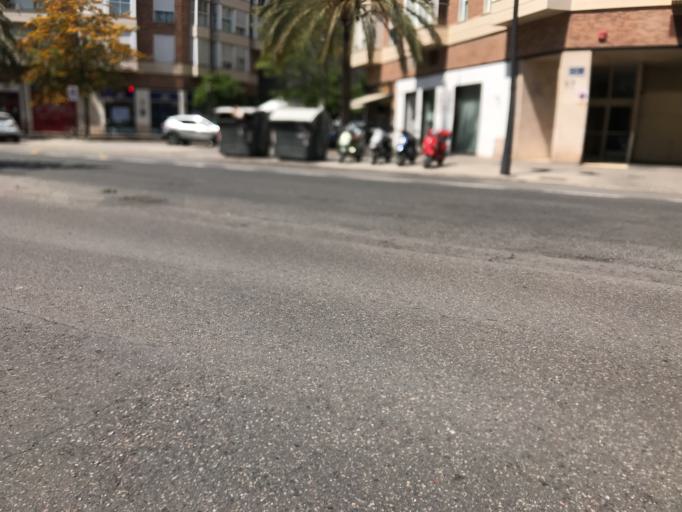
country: ES
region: Valencia
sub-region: Provincia de Valencia
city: Valencia
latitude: 39.4705
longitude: -0.3550
